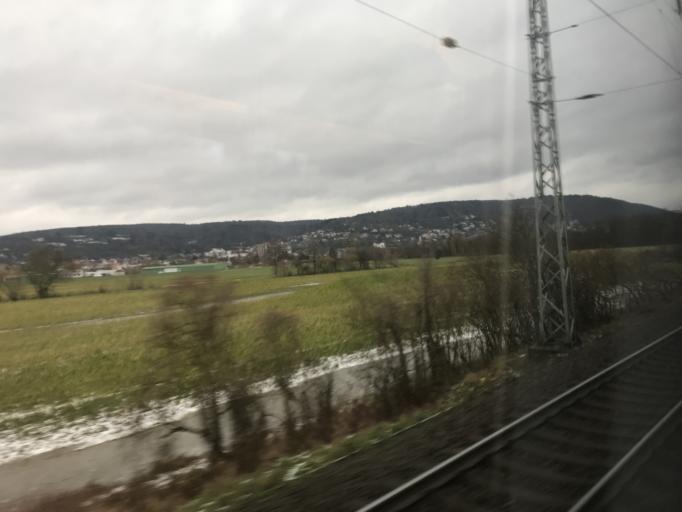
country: DE
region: Hesse
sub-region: Regierungsbezirk Darmstadt
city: Gelnhausen
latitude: 50.1935
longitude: 9.1724
